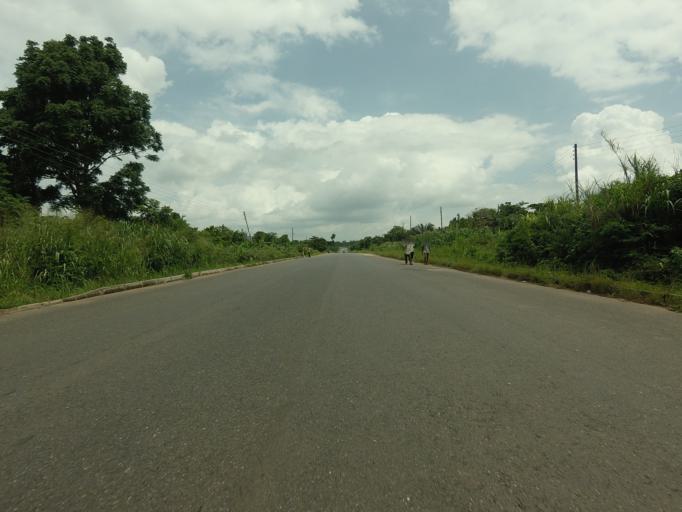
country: GH
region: Volta
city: Ho
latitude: 6.5285
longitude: 0.2256
